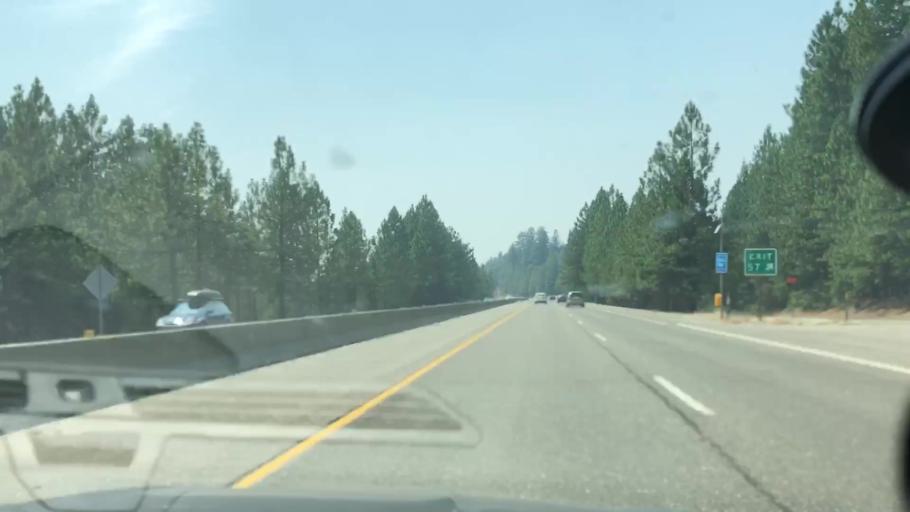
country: US
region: California
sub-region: El Dorado County
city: Pollock Pines
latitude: 38.7488
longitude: -120.6148
